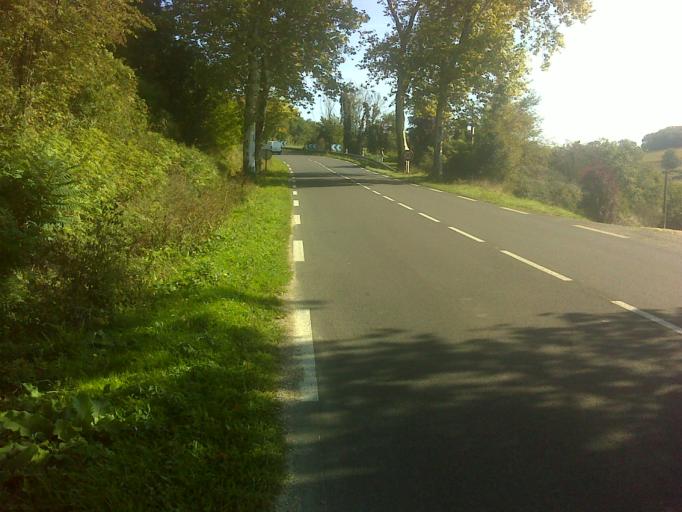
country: FR
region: Midi-Pyrenees
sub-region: Departement du Gers
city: Lectoure
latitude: 43.9270
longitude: 0.6275
